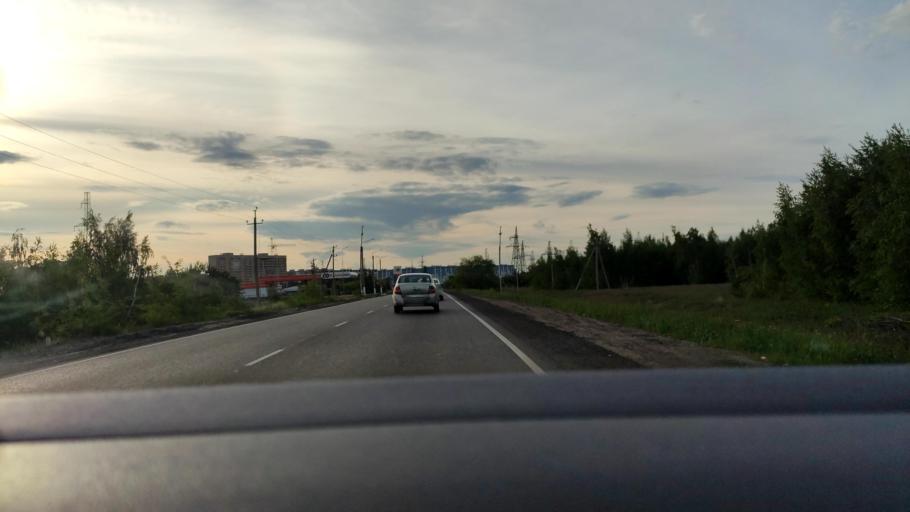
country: RU
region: Voronezj
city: Maslovka
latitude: 51.5852
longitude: 39.2563
